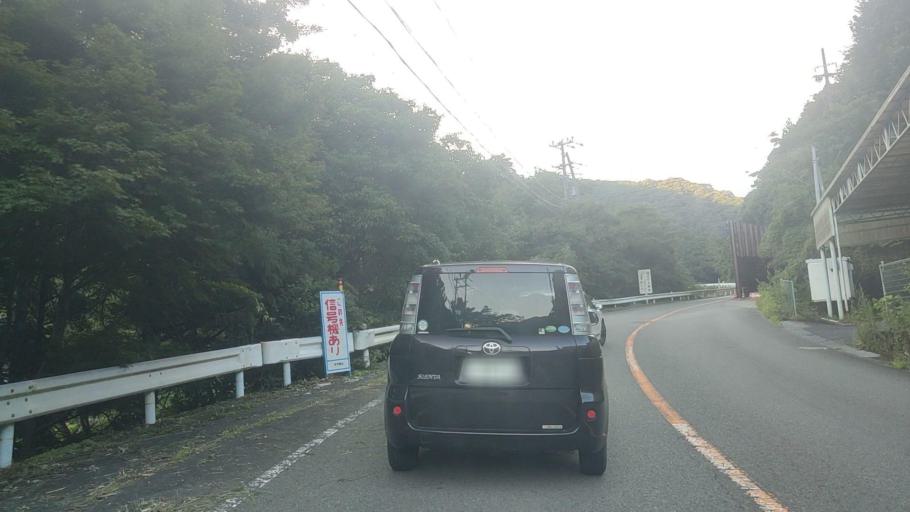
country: JP
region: Wakayama
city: Tanabe
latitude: 33.8164
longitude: 135.5538
